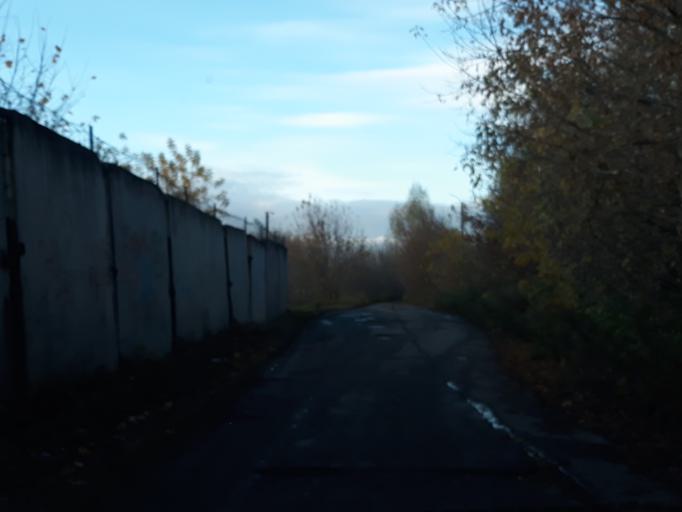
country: RU
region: Nizjnij Novgorod
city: Nizhniy Novgorod
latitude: 56.2830
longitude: 43.9698
